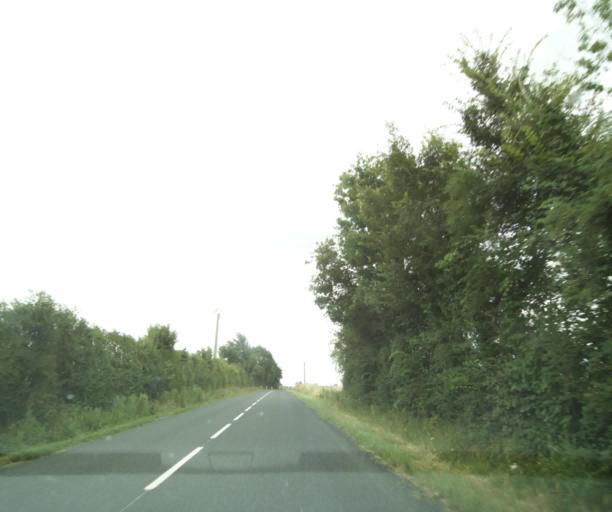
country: FR
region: Pays de la Loire
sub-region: Departement de Maine-et-Loire
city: Durtal
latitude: 47.7303
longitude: -0.2637
